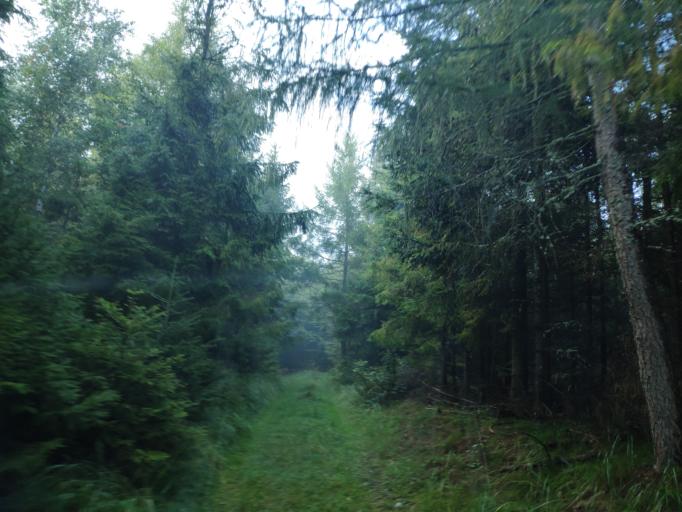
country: SK
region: Kosicky
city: Medzev
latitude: 48.7467
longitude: 20.9867
